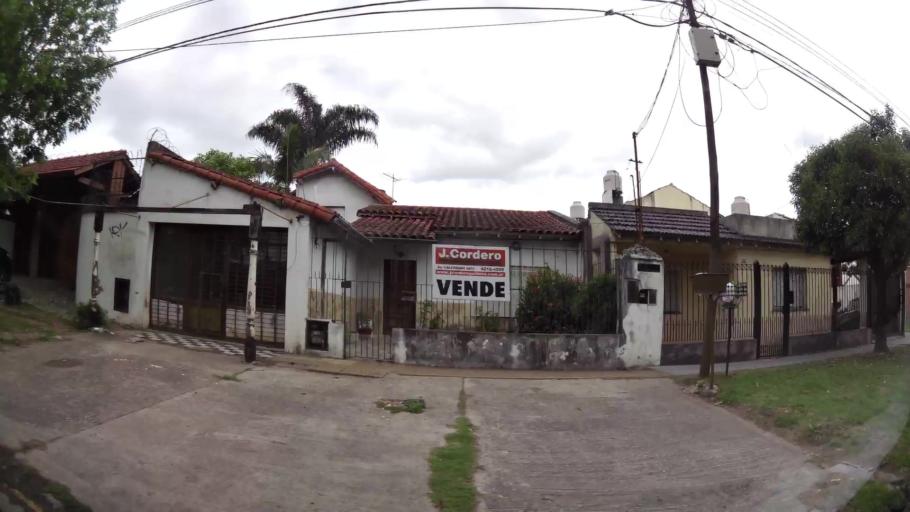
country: AR
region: Buenos Aires
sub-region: Partido de Quilmes
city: Quilmes
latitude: -34.7659
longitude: -58.2764
